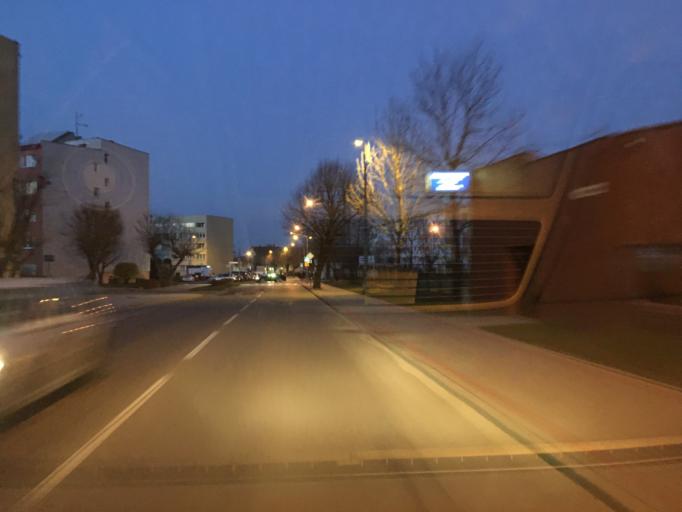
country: PL
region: Lower Silesian Voivodeship
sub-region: Powiat dzierzoniowski
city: Bielawa
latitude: 50.6889
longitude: 16.6192
